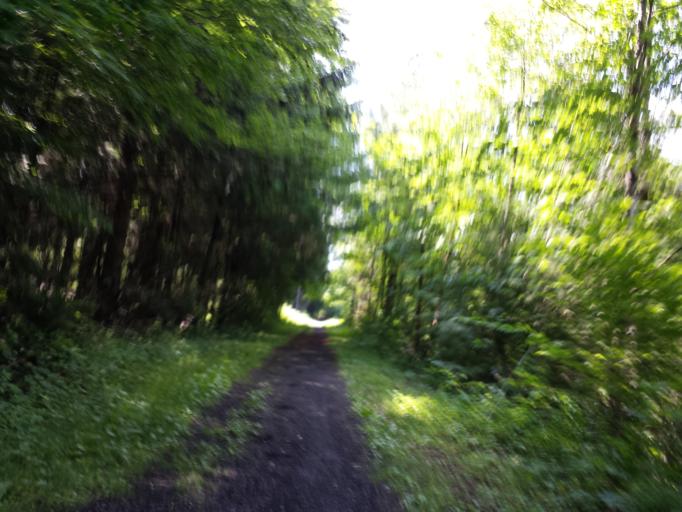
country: US
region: Vermont
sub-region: Rutland County
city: Castleton
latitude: 43.5838
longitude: -73.2023
